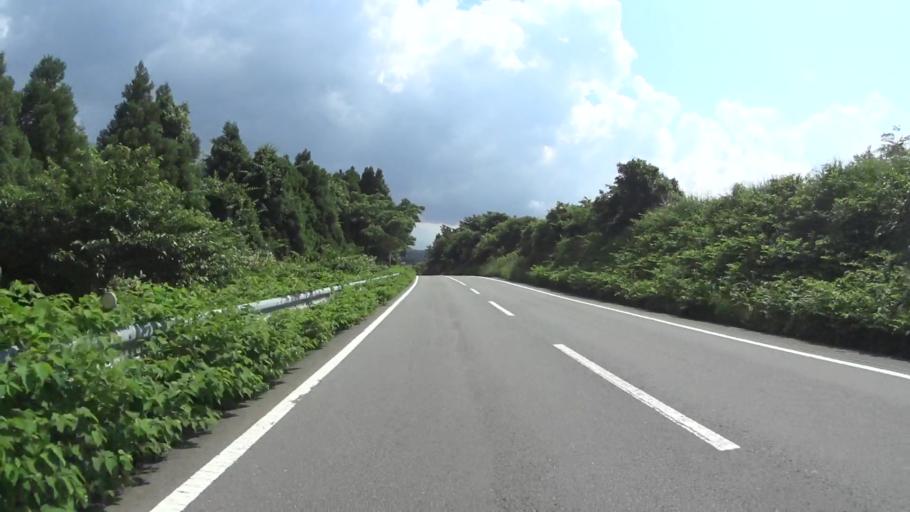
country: JP
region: Kumamoto
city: Aso
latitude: 33.0498
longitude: 131.1693
